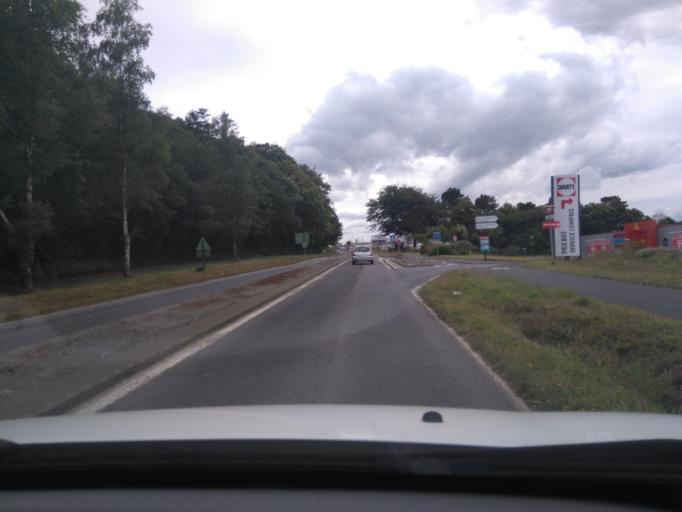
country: FR
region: Brittany
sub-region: Departement des Cotes-d'Armor
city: Saint-Quay-Perros
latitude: 48.7652
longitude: -3.4499
